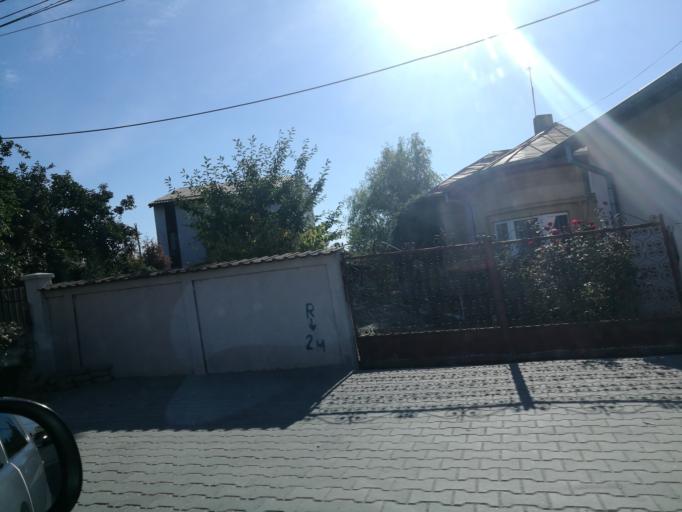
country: RO
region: Ilfov
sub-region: Comuna Dragomiresti-Vale
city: Dragomiresti-Deal
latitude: 44.4569
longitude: 25.9500
